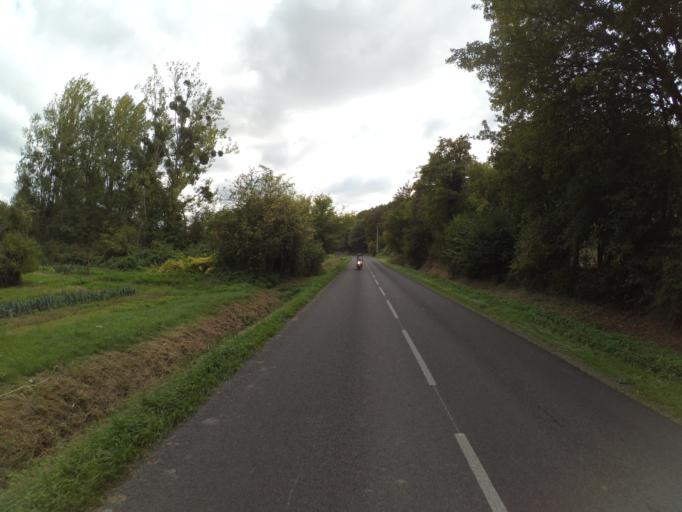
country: FR
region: Centre
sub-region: Departement d'Indre-et-Loire
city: Reugny
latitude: 47.4679
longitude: 0.8797
